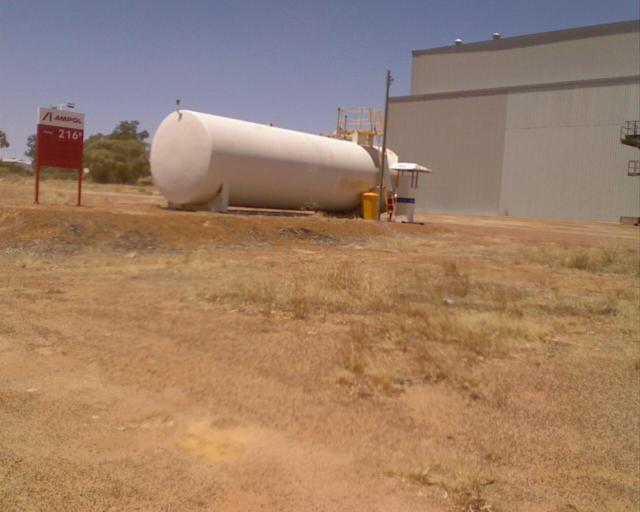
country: AU
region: Western Australia
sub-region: Merredin
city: Merredin
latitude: -30.8159
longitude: 117.8632
